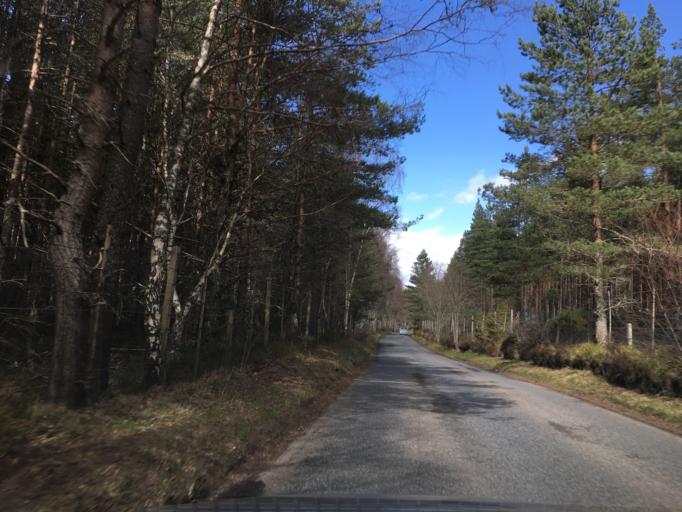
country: GB
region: Scotland
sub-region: Highland
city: Aviemore
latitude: 57.1966
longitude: -3.7986
